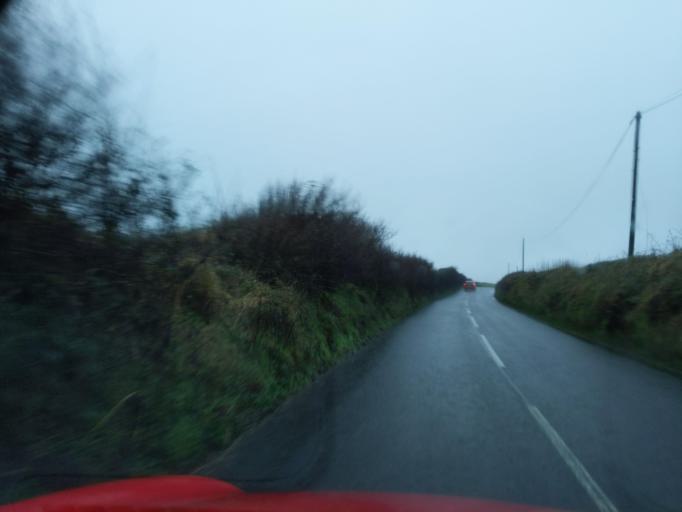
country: GB
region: England
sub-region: Cornwall
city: Camelford
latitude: 50.6398
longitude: -4.6936
